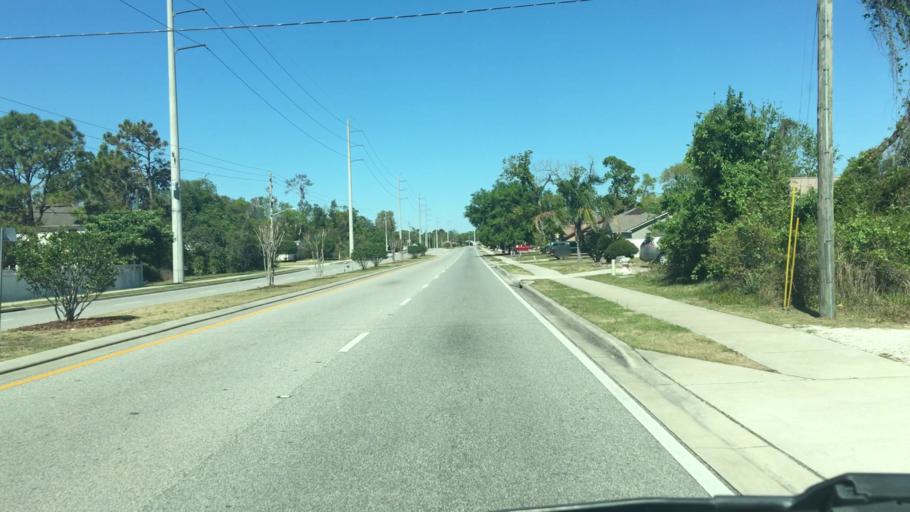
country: US
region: Florida
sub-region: Volusia County
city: Deltona
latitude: 28.9047
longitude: -81.1741
